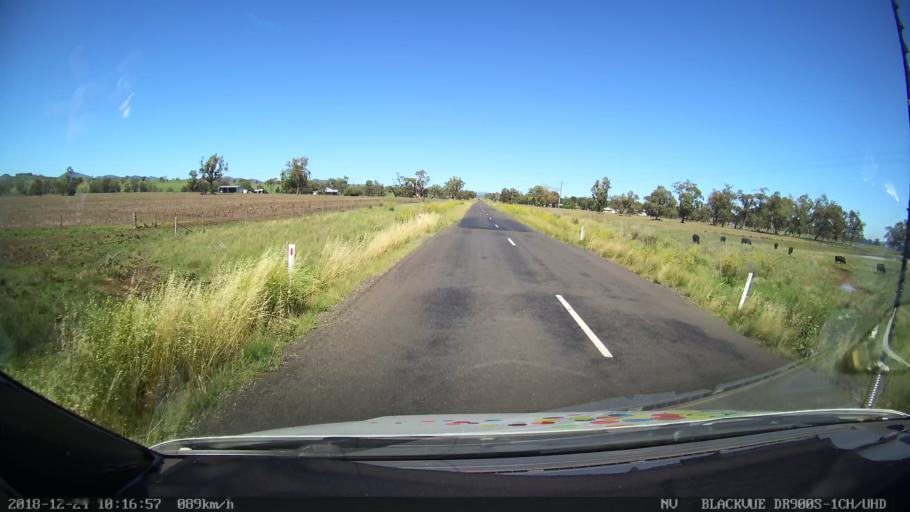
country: AU
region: New South Wales
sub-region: Liverpool Plains
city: Quirindi
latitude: -31.7182
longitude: 150.5984
